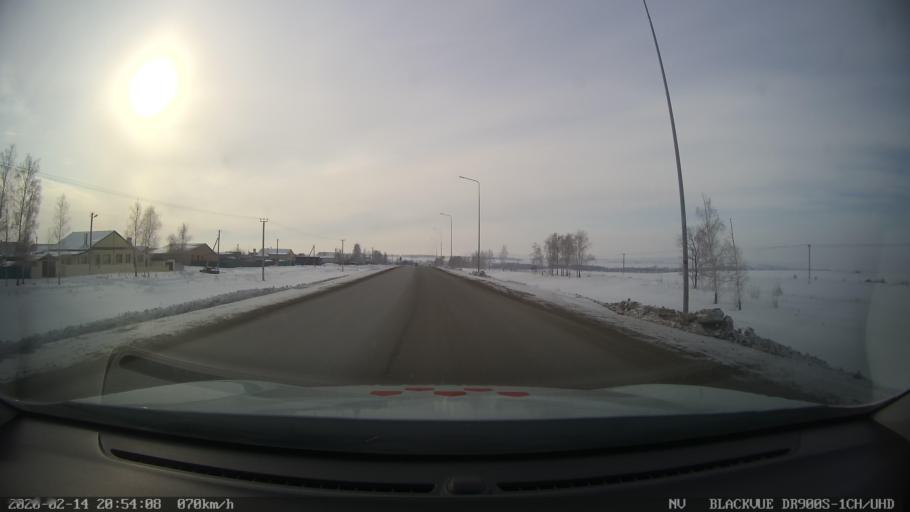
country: RU
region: Tatarstan
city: Kuybyshevskiy Zaton
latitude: 55.1886
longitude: 49.2452
